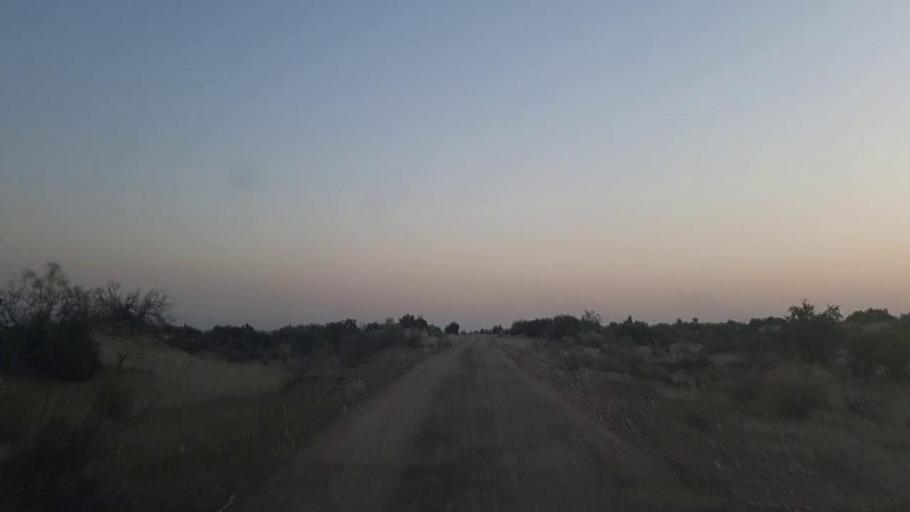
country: PK
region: Sindh
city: Jam Sahib
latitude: 26.4163
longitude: 68.8095
